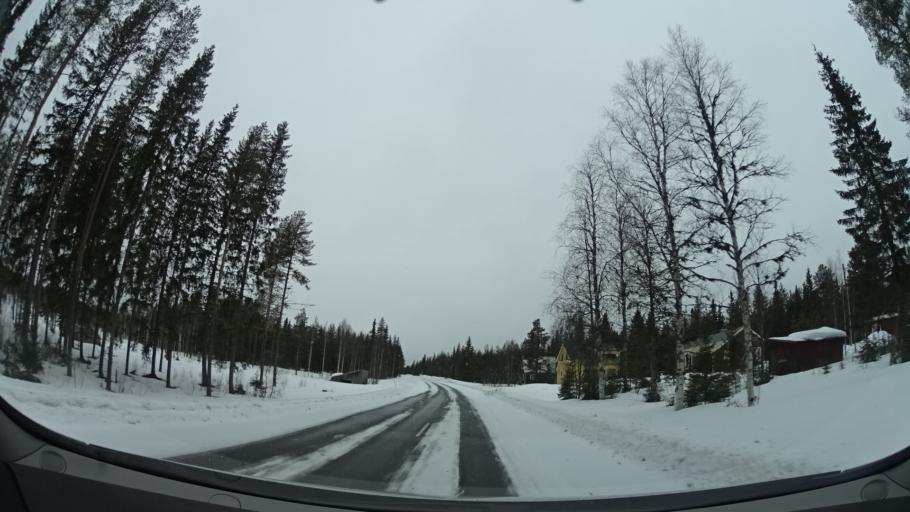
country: SE
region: Vaesterbotten
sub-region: Mala Kommun
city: Mala
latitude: 65.0825
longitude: 18.9951
